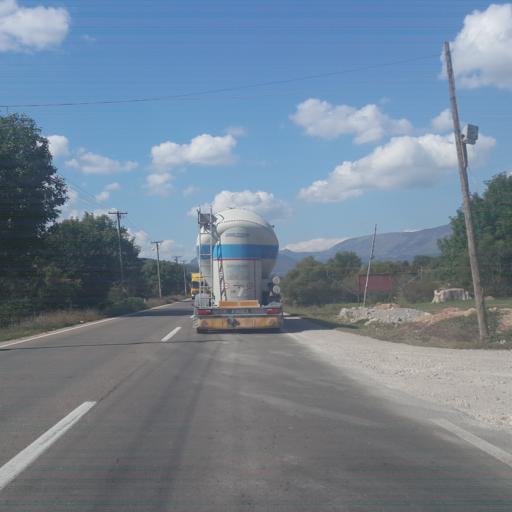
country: RS
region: Central Serbia
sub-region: Pirotski Okrug
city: Bela Palanka
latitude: 43.2666
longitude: 22.2477
